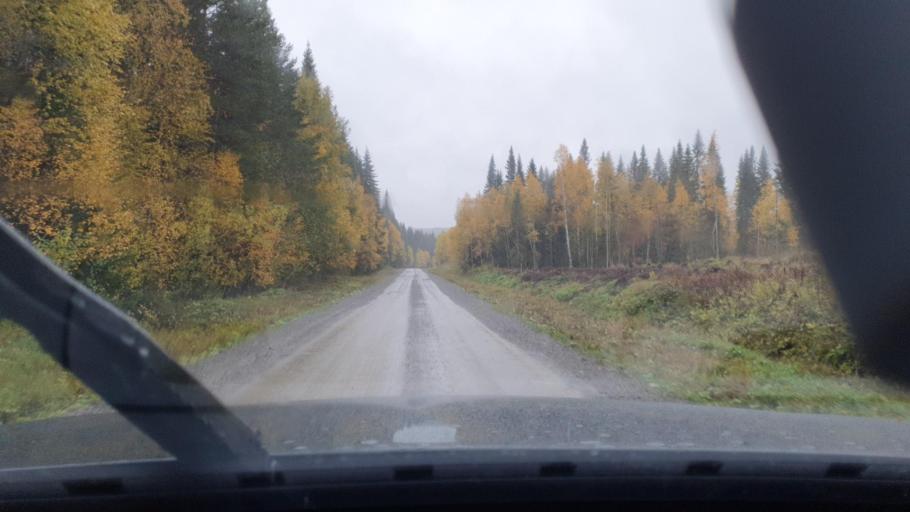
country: SE
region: Jaemtland
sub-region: Stroemsunds Kommun
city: Stroemsund
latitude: 63.5155
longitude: 15.6485
